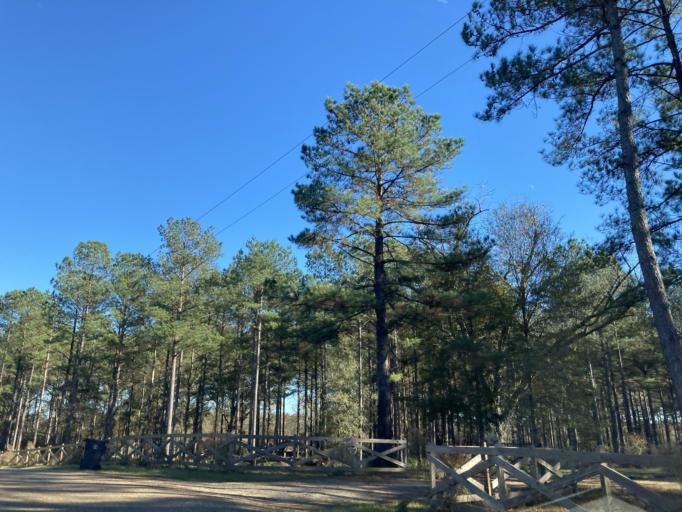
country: US
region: Mississippi
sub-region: Lamar County
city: Sumrall
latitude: 31.3316
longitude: -89.6262
